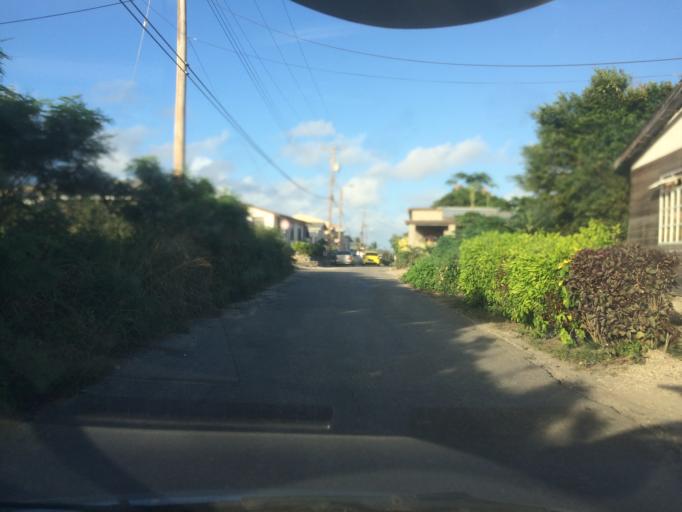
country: BB
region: Saint Lucy
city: Checker Hall
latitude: 13.3263
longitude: -59.6159
